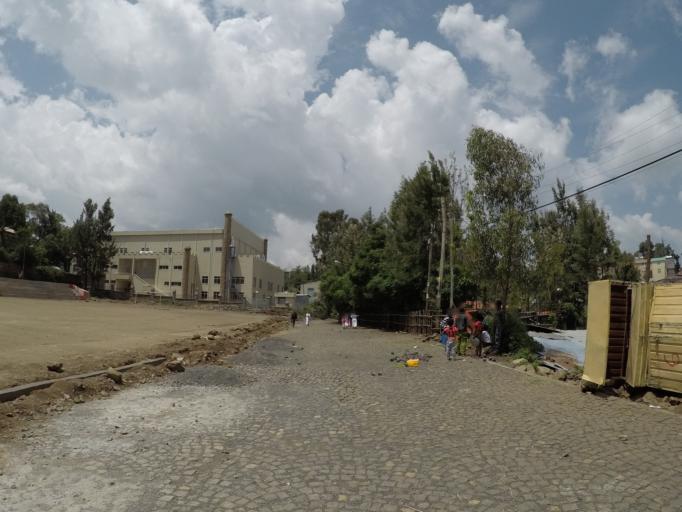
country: ET
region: Amhara
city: Gondar
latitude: 12.6129
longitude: 37.4726
